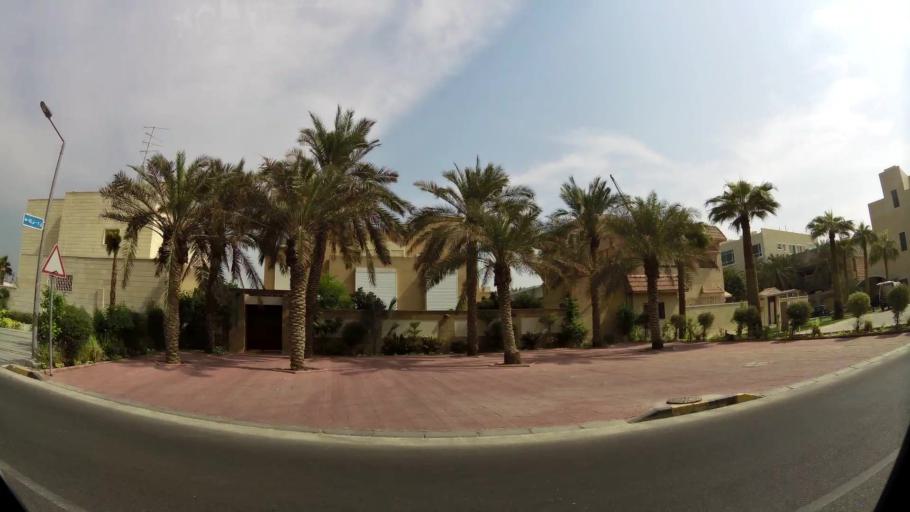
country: KW
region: Al Asimah
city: Kuwait City
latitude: 29.3562
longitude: 47.9763
